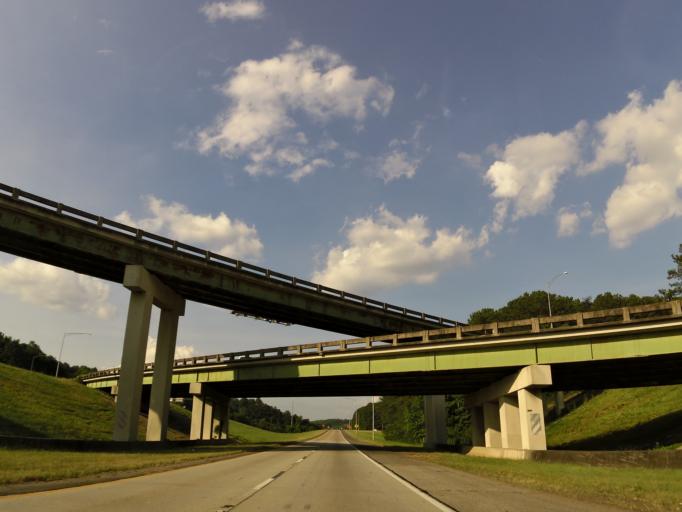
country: US
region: Alabama
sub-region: Jefferson County
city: Trussville
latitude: 33.5978
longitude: -86.6547
